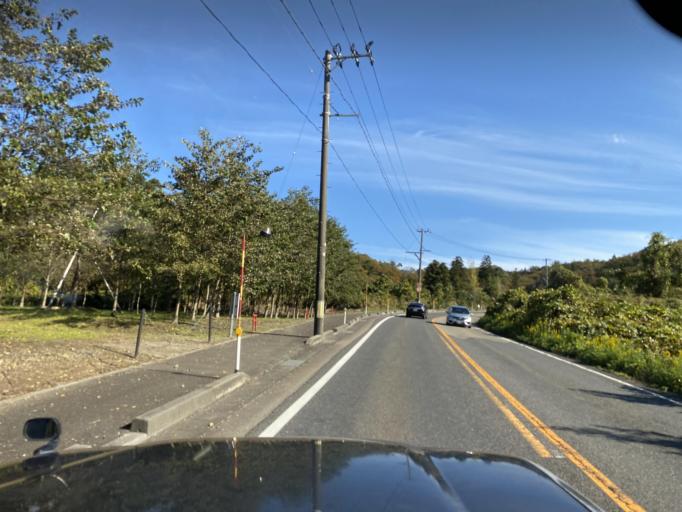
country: JP
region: Niigata
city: Niitsu-honcho
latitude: 37.7507
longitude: 139.1054
